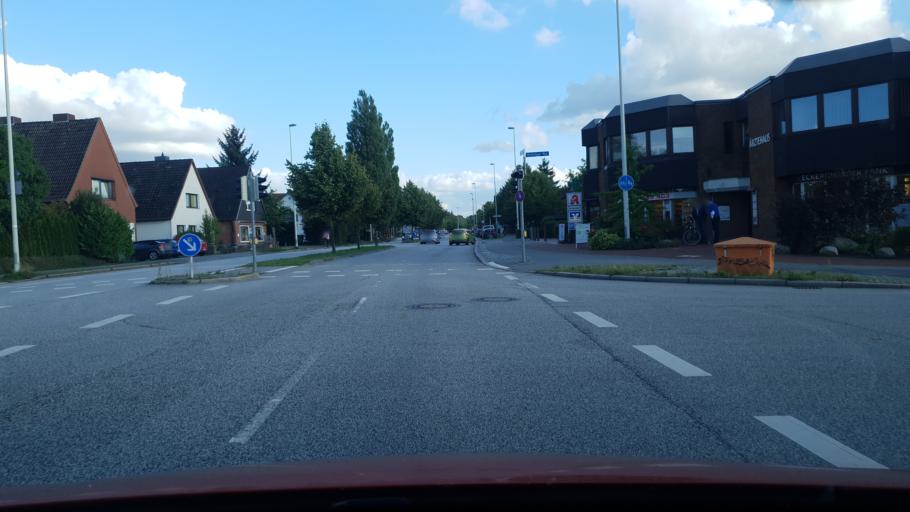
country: DE
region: Schleswig-Holstein
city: Kronshagen
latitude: 54.3554
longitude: 10.0860
